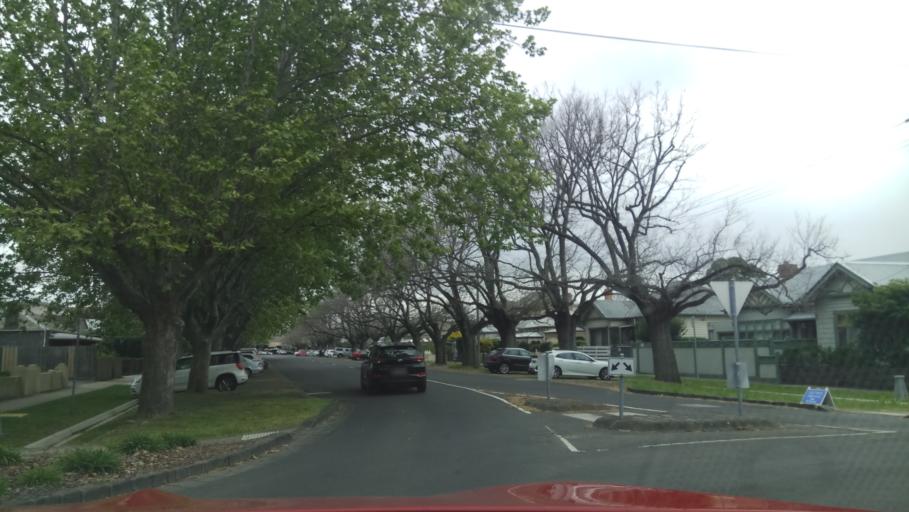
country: AU
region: Victoria
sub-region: Hobsons Bay
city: Williamstown
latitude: -37.8616
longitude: 144.8984
